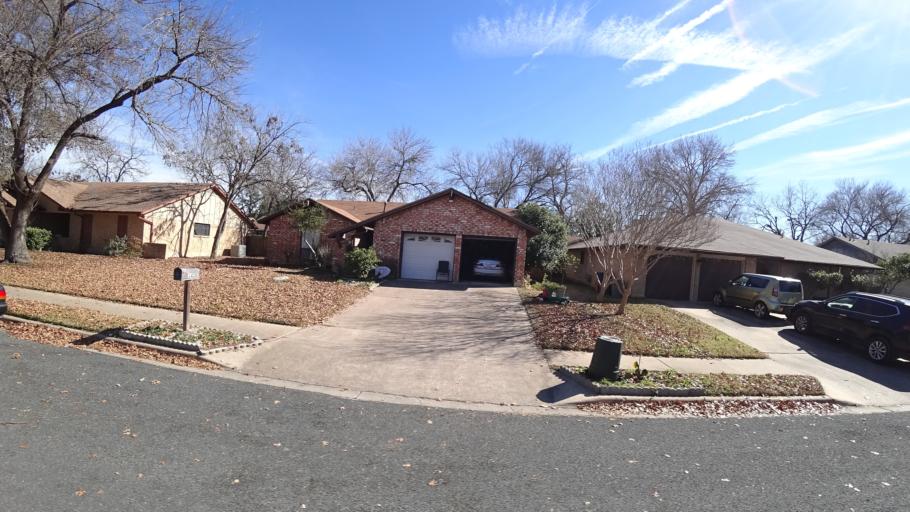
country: US
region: Texas
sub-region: Travis County
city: Wells Branch
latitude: 30.3802
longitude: -97.7005
